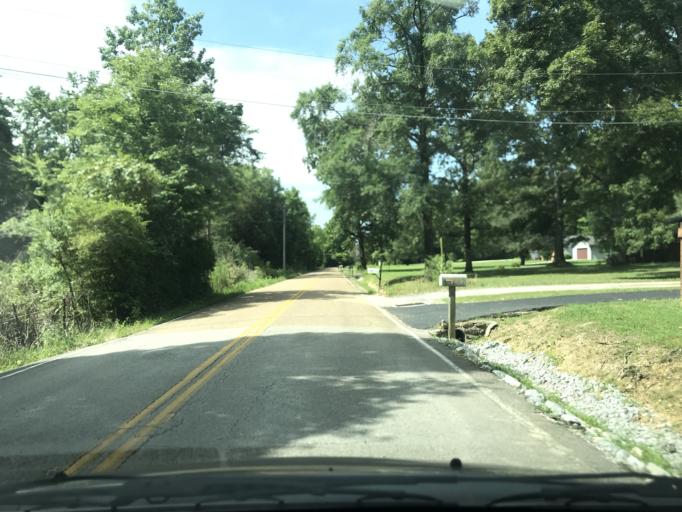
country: US
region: Tennessee
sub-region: Hamilton County
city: Lakesite
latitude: 35.1729
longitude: -85.0628
